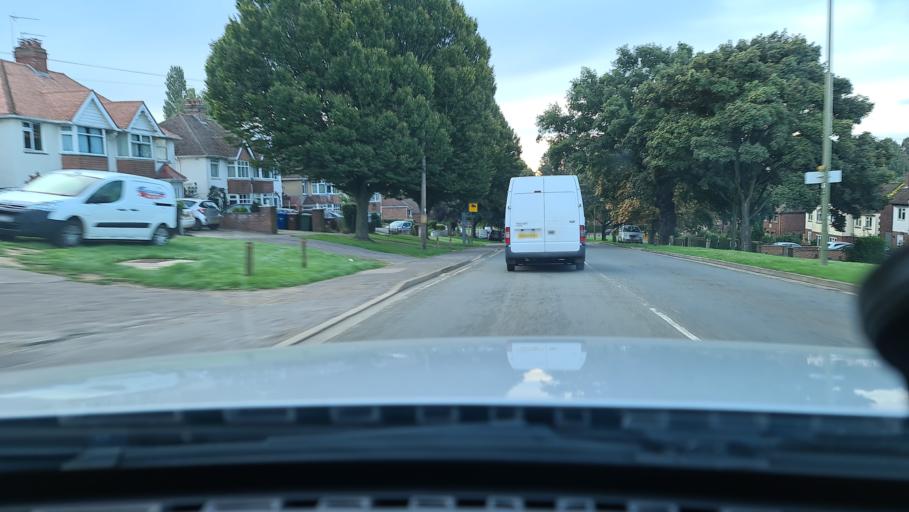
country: GB
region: England
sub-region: Oxfordshire
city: Banbury
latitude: 52.0677
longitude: -1.3583
